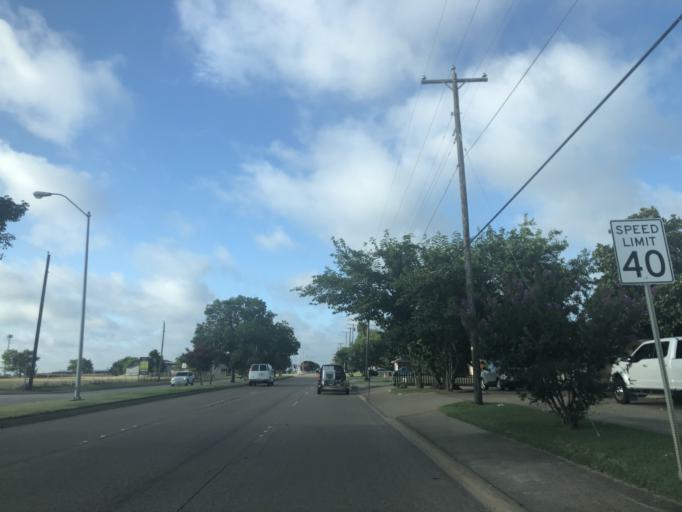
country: US
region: Texas
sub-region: Dallas County
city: Duncanville
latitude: 32.6734
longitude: -96.9087
